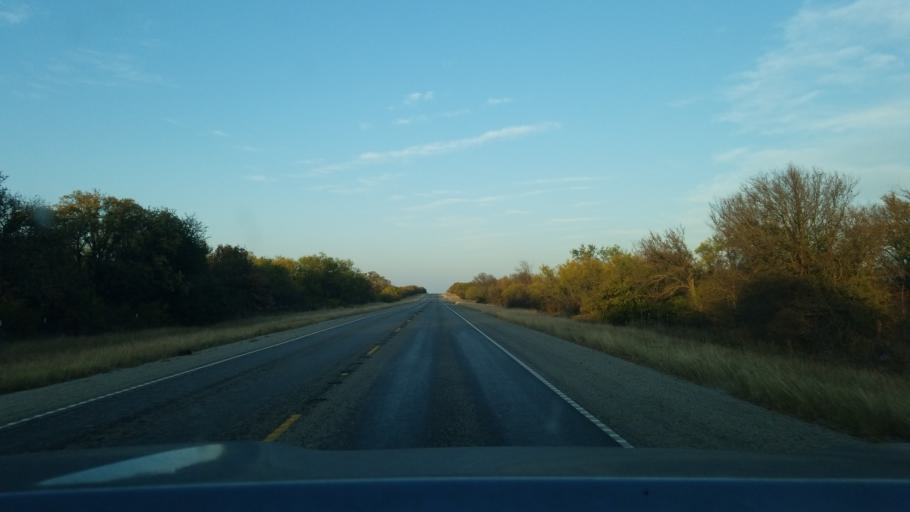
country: US
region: Texas
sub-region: Eastland County
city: Cisco
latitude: 32.4242
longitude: -98.9333
